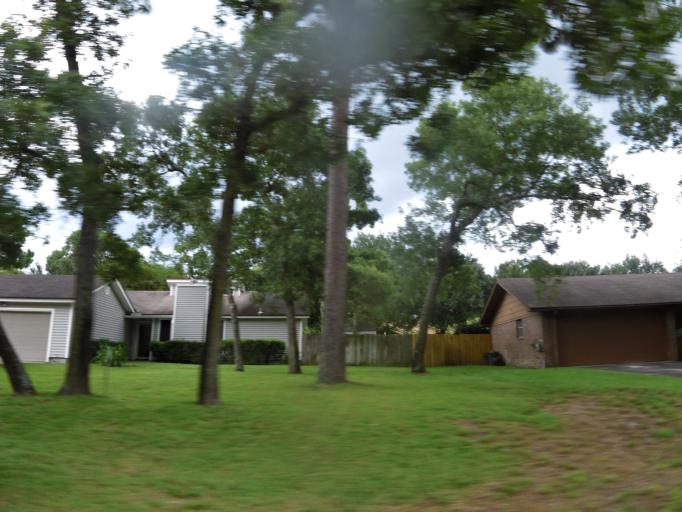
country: US
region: Florida
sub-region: Duval County
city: Atlantic Beach
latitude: 30.3577
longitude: -81.5121
